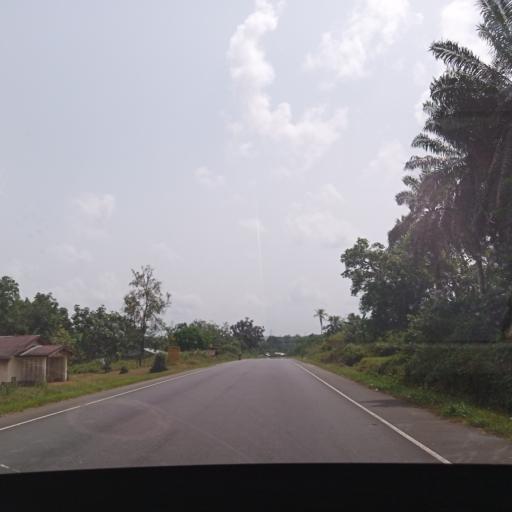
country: LR
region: Margibi
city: Kakata
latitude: 6.2325
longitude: -10.2805
